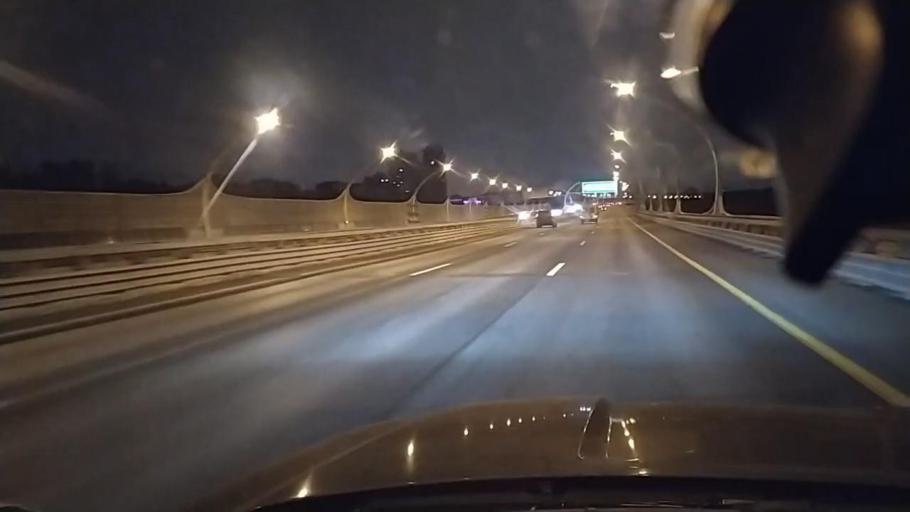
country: RU
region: Leningrad
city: Untolovo
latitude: 60.0260
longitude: 30.2079
